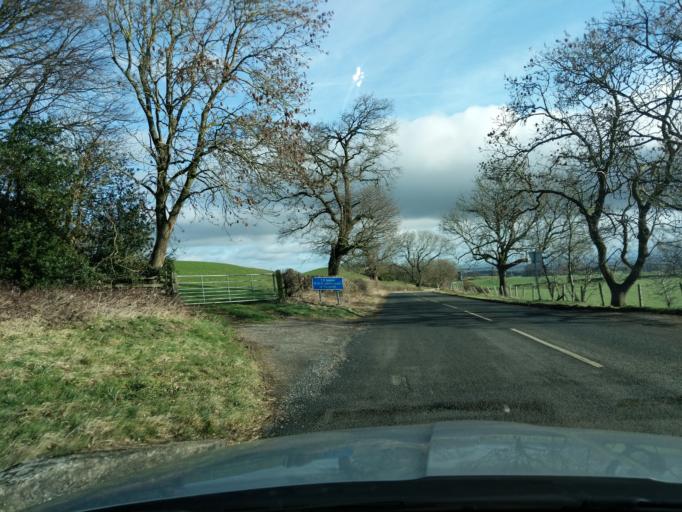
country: GB
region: England
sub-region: North Yorkshire
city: Catterick Garrison
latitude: 54.3480
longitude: -1.6939
